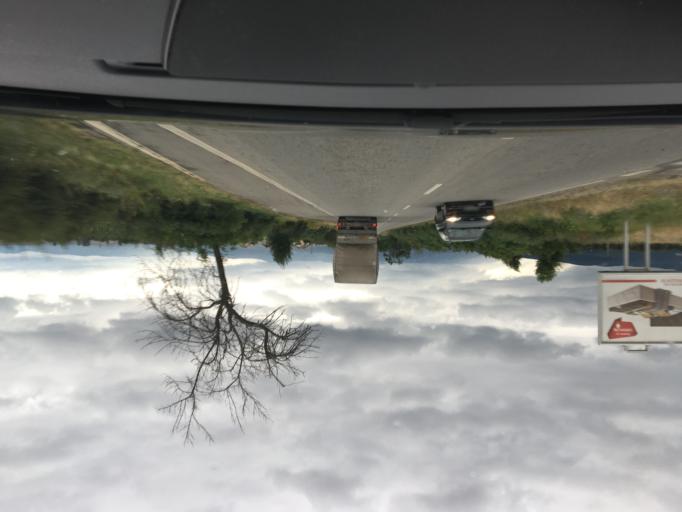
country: BG
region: Kyustendil
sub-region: Obshtina Kyustendil
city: Kyustendil
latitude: 42.2731
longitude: 22.7659
